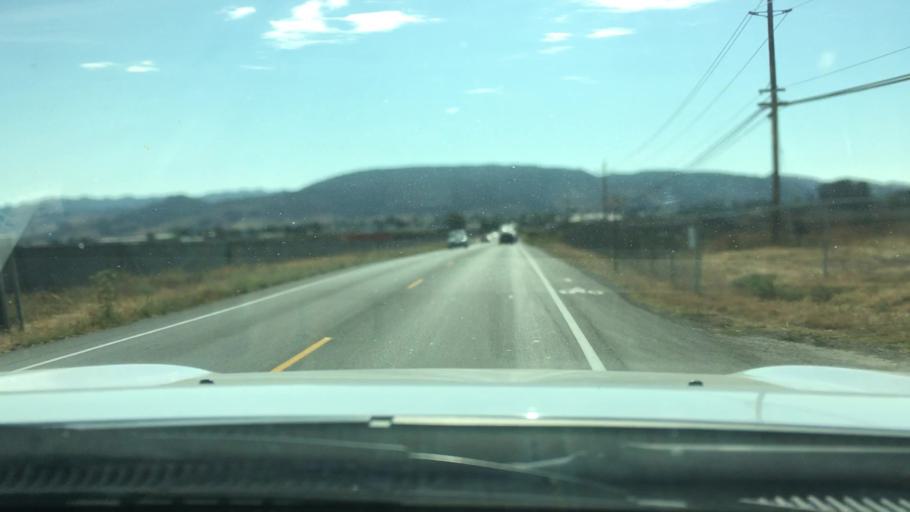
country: US
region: California
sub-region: San Luis Obispo County
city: San Luis Obispo
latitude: 35.2466
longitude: -120.6555
